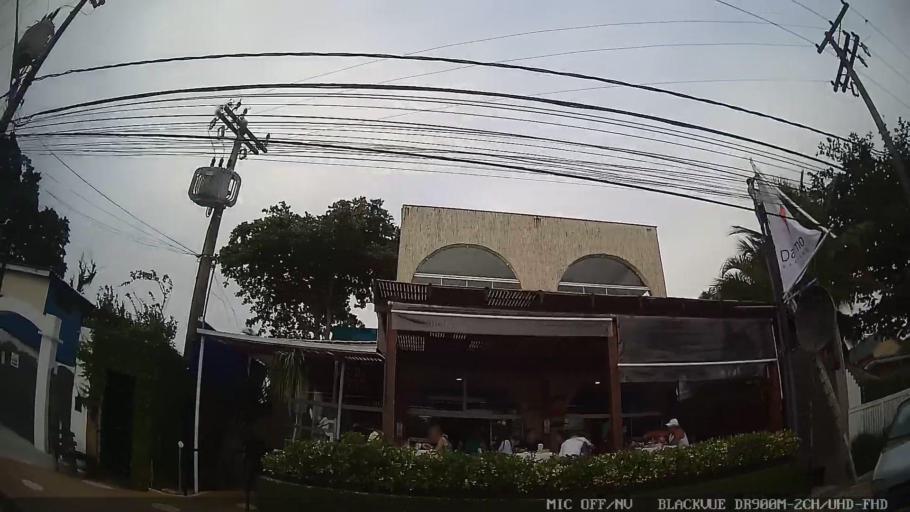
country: BR
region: Sao Paulo
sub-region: Guaruja
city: Guaruja
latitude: -23.9877
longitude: -46.2053
